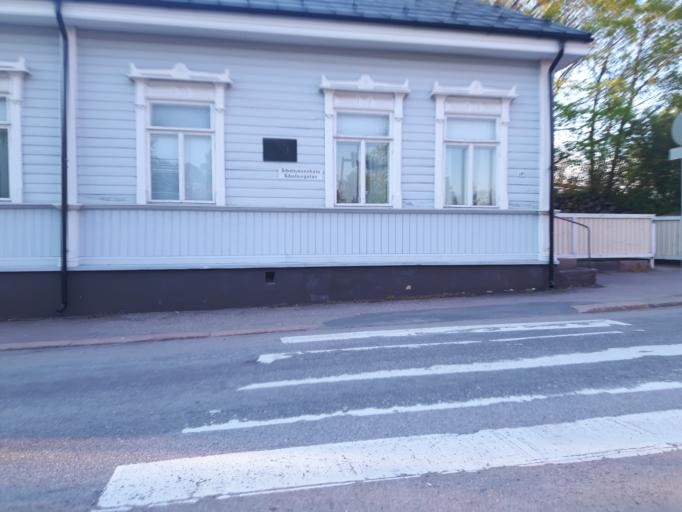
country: FI
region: Uusimaa
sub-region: Loviisa
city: Lovisa
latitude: 60.4565
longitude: 26.2219
